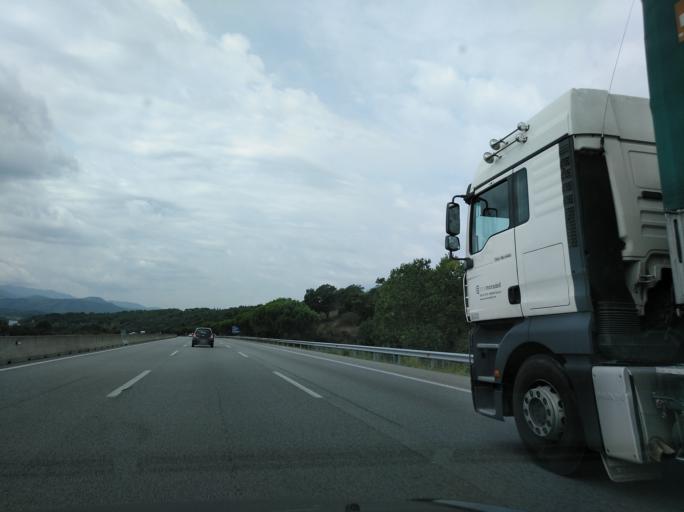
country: ES
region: Catalonia
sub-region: Provincia de Girona
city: Macanet de la Selva
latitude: 41.7614
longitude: 2.7208
